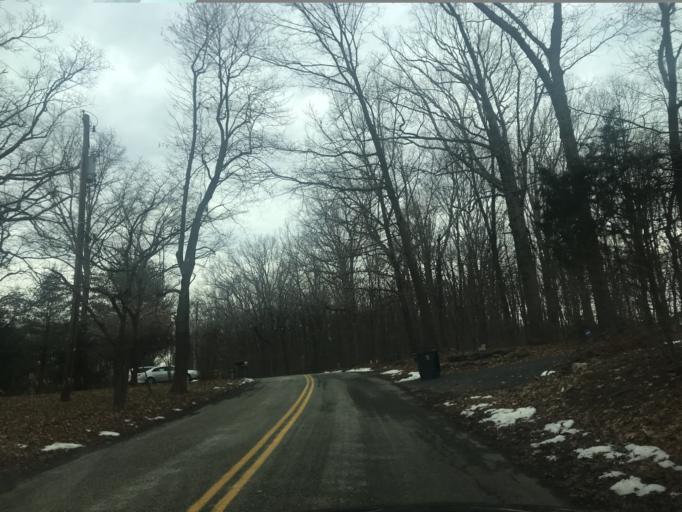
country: US
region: Maryland
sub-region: Harford County
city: Jarrettsville
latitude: 39.6538
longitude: -76.4054
